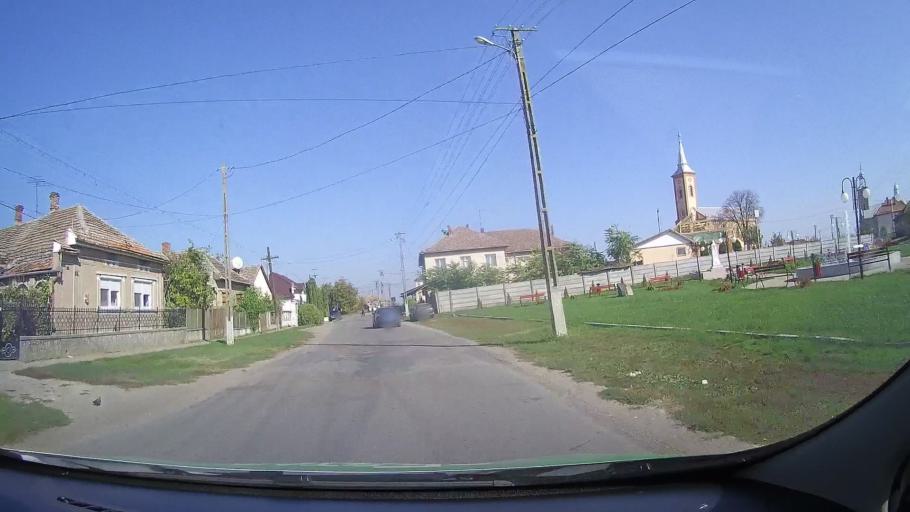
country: RO
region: Satu Mare
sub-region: Comuna Sanislau
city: Sanislau
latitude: 47.6407
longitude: 22.3253
